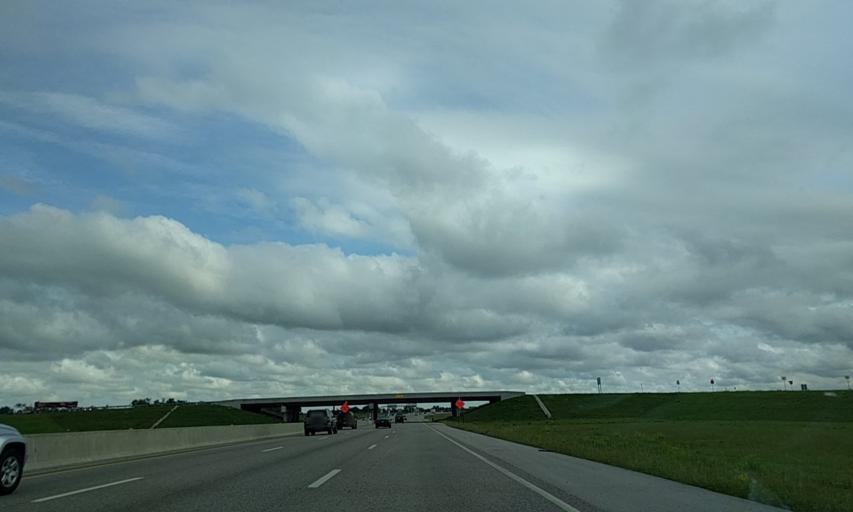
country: US
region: Oklahoma
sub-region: Tulsa County
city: Owasso
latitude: 36.2188
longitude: -95.8516
